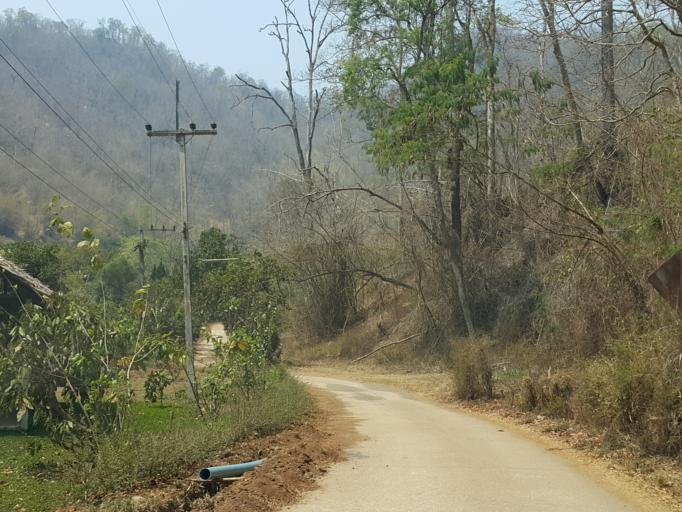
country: TH
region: Chiang Mai
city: Samoeng
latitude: 18.7914
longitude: 98.8101
